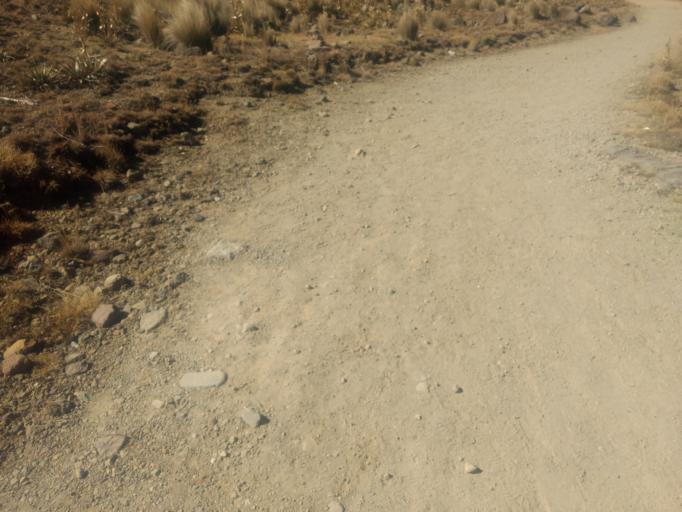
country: MX
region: Mexico
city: Cerro La Calera
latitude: 19.1082
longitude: -99.7610
